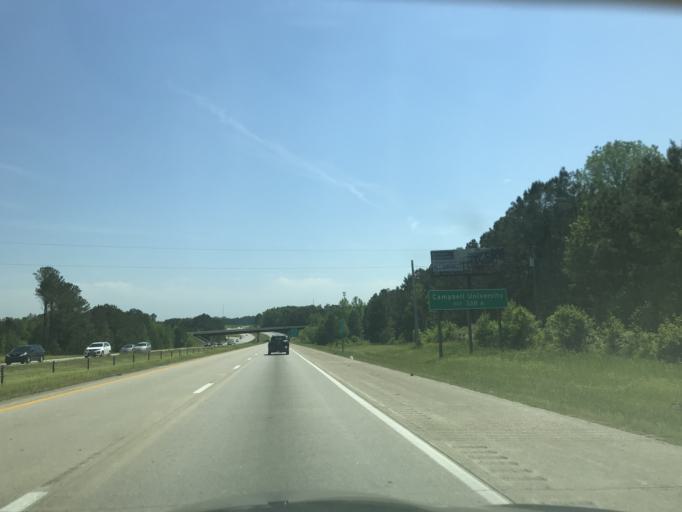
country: US
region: North Carolina
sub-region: Johnston County
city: Benson
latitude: 35.4014
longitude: -78.5232
